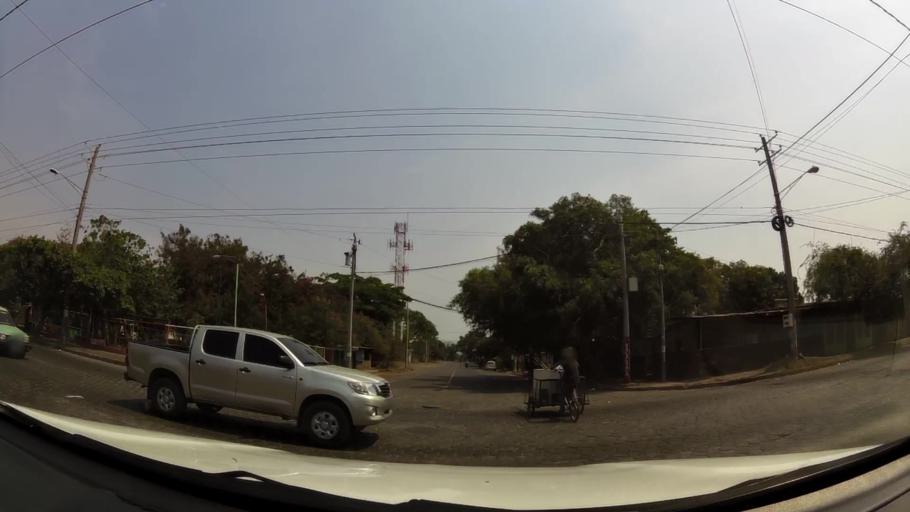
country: NI
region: Managua
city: Ciudad Sandino
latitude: 12.1579
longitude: -86.2970
